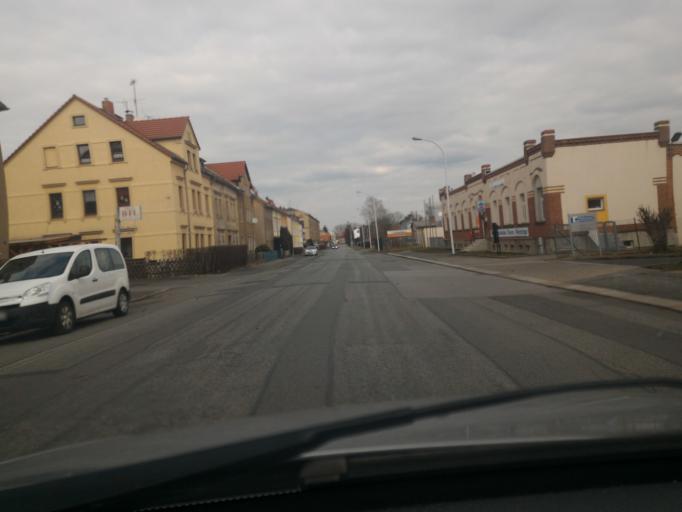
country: DE
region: Saxony
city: Zittau
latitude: 50.8800
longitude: 14.8125
